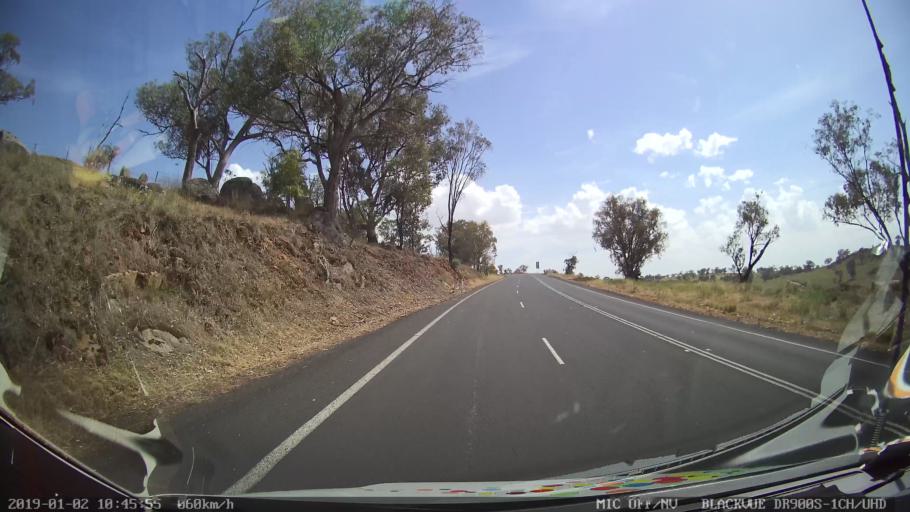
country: AU
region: New South Wales
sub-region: Cootamundra
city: Cootamundra
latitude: -34.7563
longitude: 148.2882
